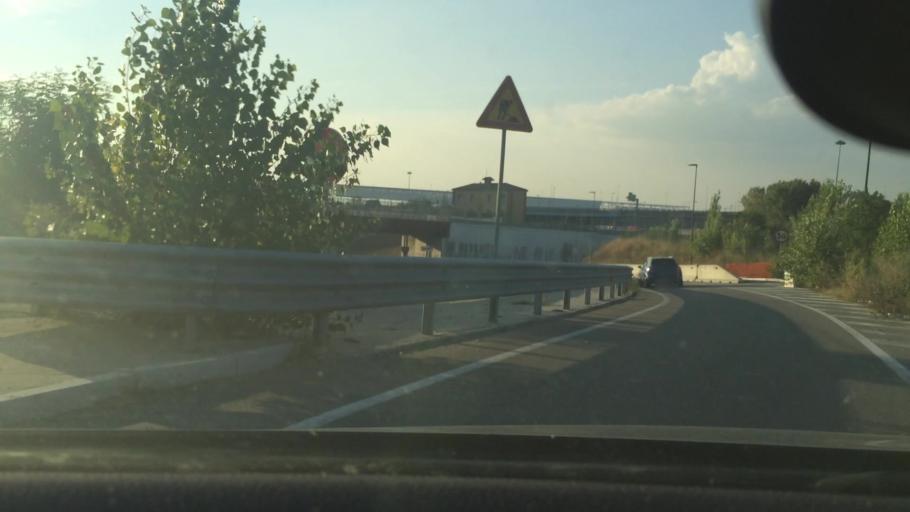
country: IT
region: Lombardy
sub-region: Citta metropolitana di Milano
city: Baranzate
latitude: 45.5121
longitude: 9.1067
